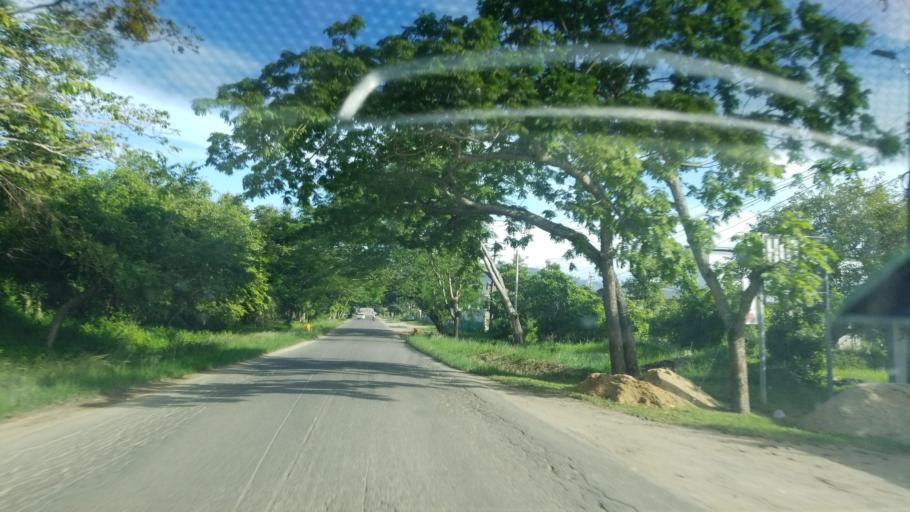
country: HN
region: El Paraiso
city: Cuyali
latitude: 13.8916
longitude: -86.5551
